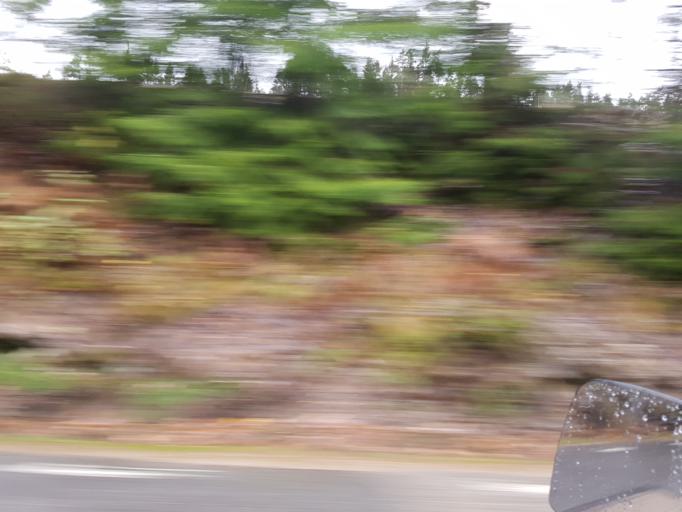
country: SE
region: Vaestra Goetaland
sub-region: Orust
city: Henan
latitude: 58.2657
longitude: 11.7368
